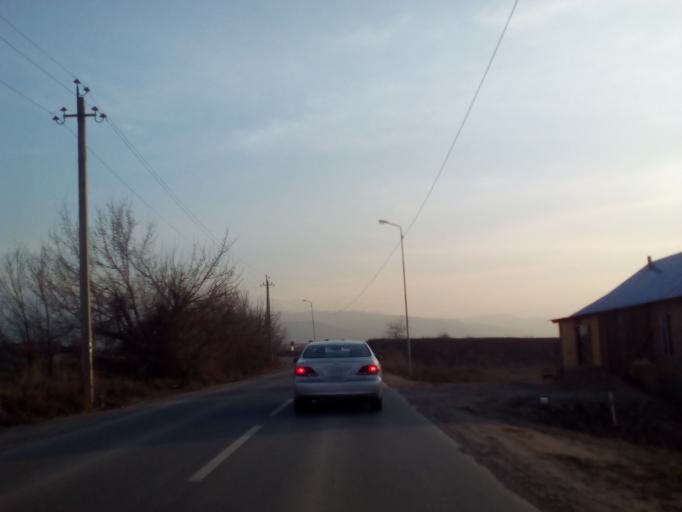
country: KZ
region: Almaty Oblysy
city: Burunday
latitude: 43.2350
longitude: 76.7412
